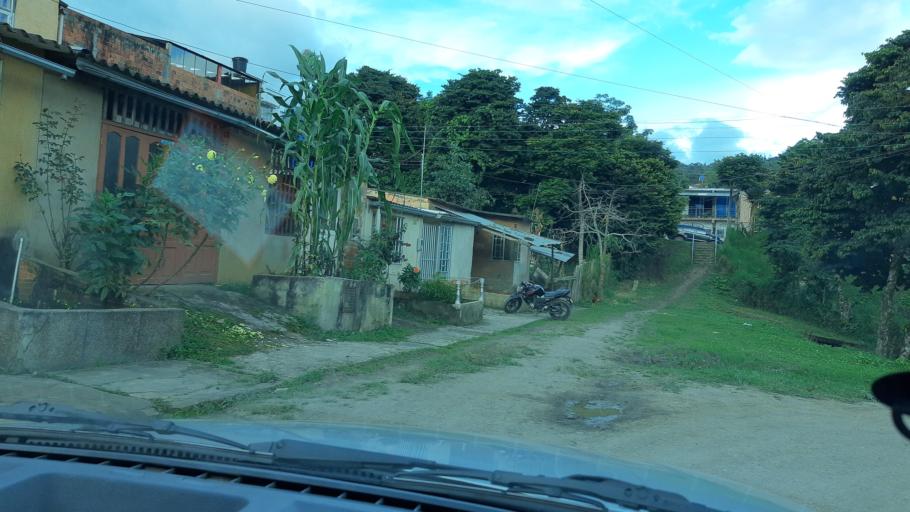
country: CO
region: Boyaca
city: Garagoa
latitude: 5.0858
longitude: -73.3662
